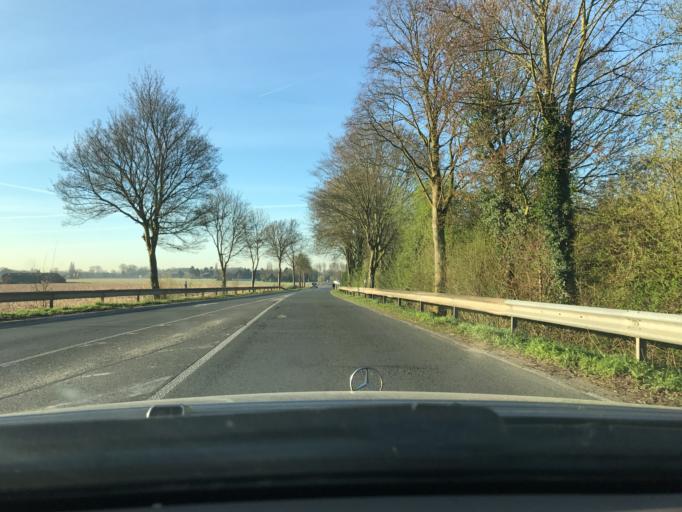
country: DE
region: North Rhine-Westphalia
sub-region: Regierungsbezirk Dusseldorf
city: Krefeld
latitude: 51.3966
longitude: 6.5996
